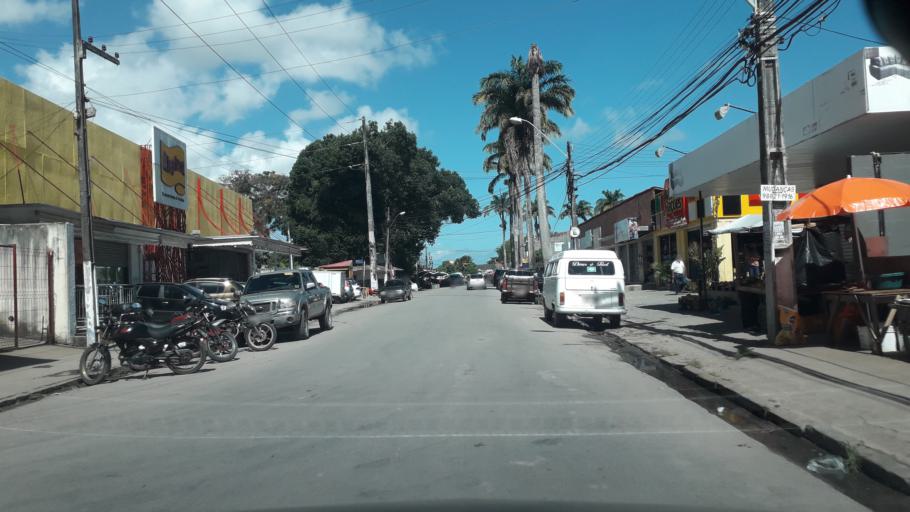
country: BR
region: Alagoas
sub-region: Satuba
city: Satuba
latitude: -9.5826
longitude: -35.7691
